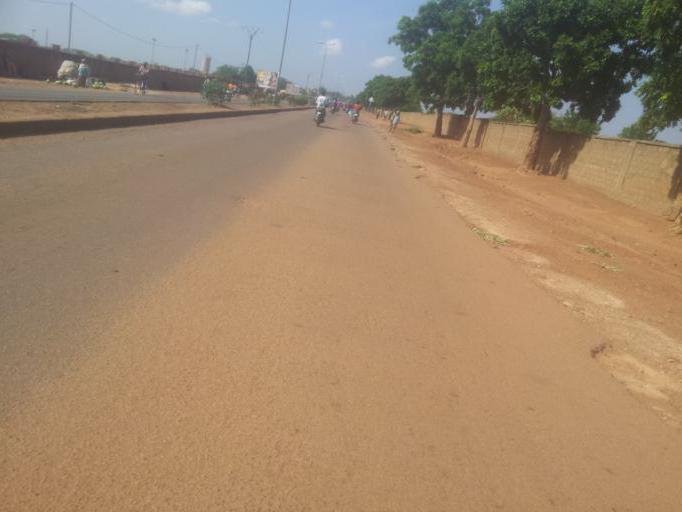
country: BF
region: Centre
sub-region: Kadiogo Province
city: Ouagadougou
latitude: 12.3678
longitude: -1.5586
